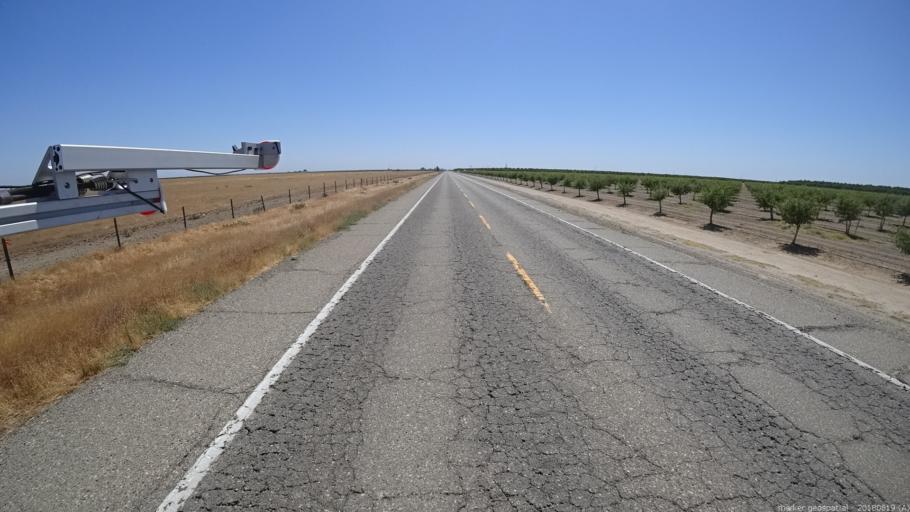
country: US
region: California
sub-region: Fresno County
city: Mendota
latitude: 36.8510
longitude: -120.2319
